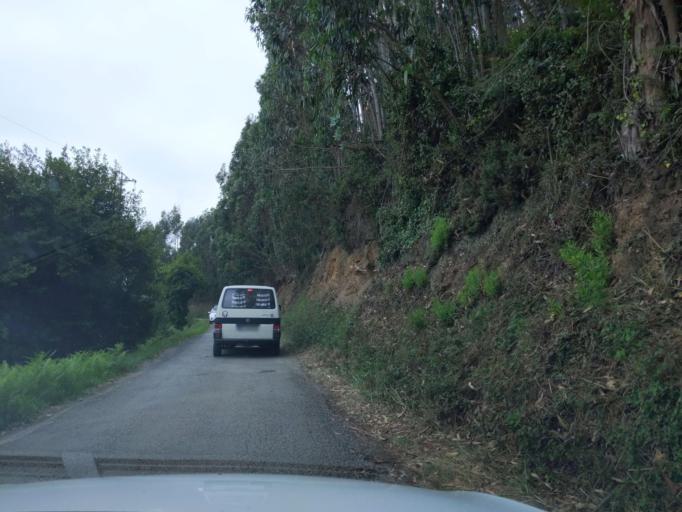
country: ES
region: Asturias
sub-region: Province of Asturias
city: Aviles
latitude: 43.6007
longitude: -5.9102
